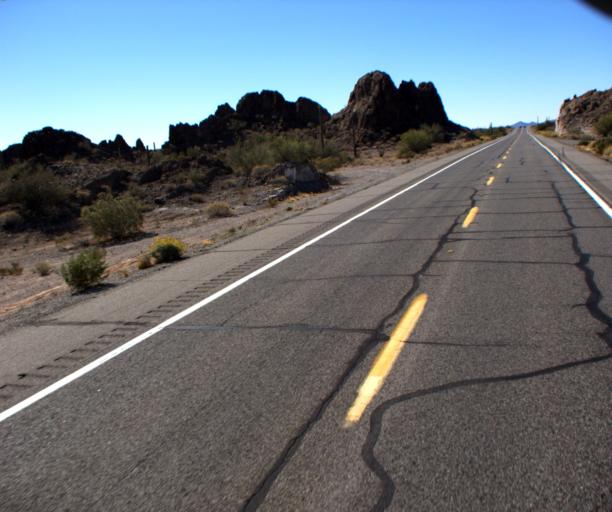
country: US
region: Arizona
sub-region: Pima County
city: Ajo
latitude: 32.5464
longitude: -112.8800
